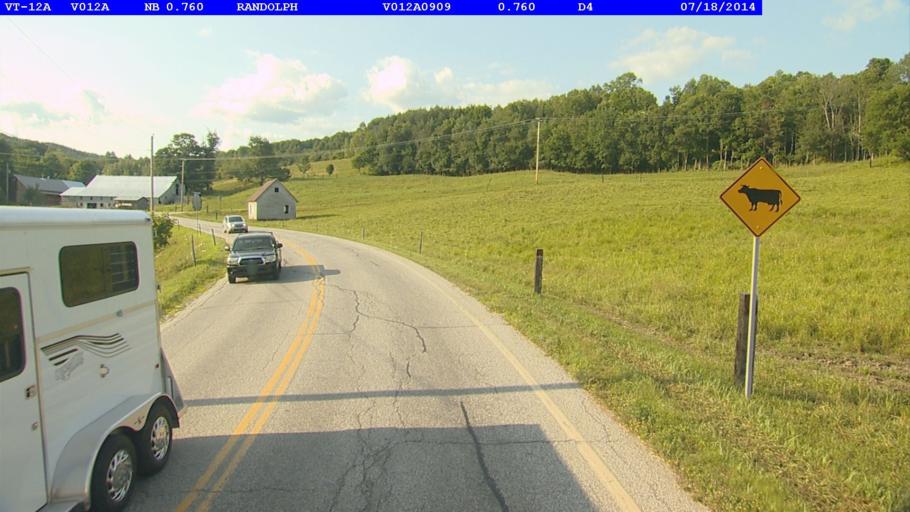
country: US
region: Vermont
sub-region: Orange County
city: Randolph
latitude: 43.9301
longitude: -72.6784
